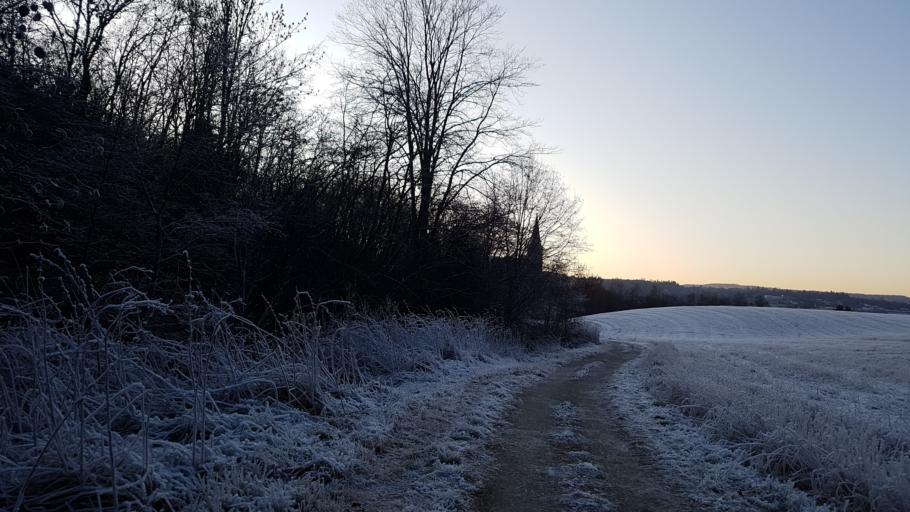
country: NO
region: Sor-Trondelag
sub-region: Melhus
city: Melhus
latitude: 63.2743
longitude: 10.2992
